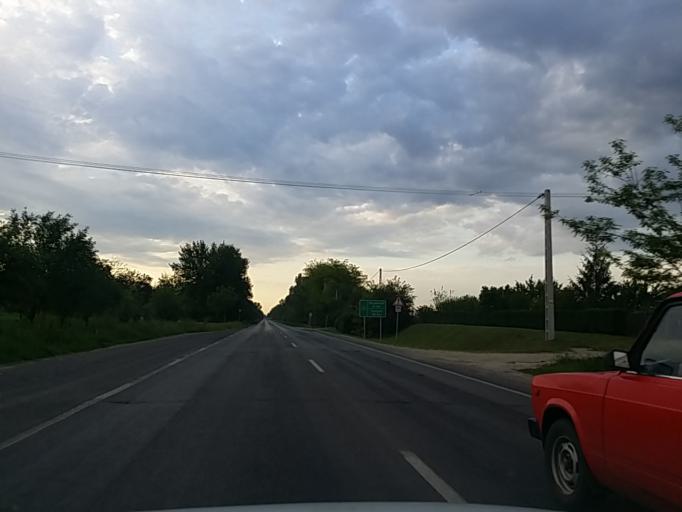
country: HU
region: Bacs-Kiskun
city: Lajosmizse
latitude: 47.0159
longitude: 19.5735
